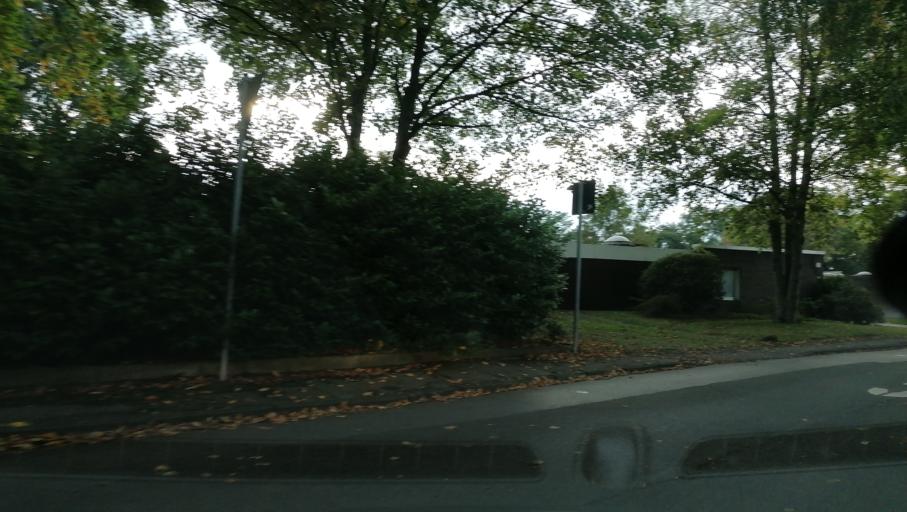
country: DE
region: North Rhine-Westphalia
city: Herten
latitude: 51.5739
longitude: 7.1079
